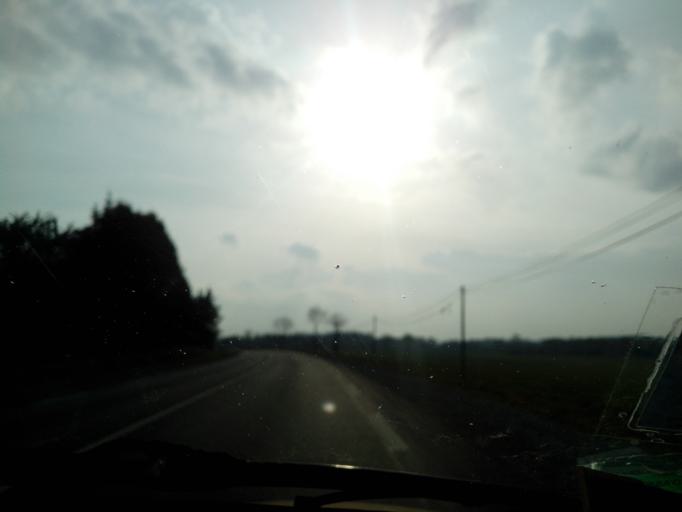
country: FR
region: Brittany
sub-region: Departement du Morbihan
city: Mauron
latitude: 48.0690
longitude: -2.2881
